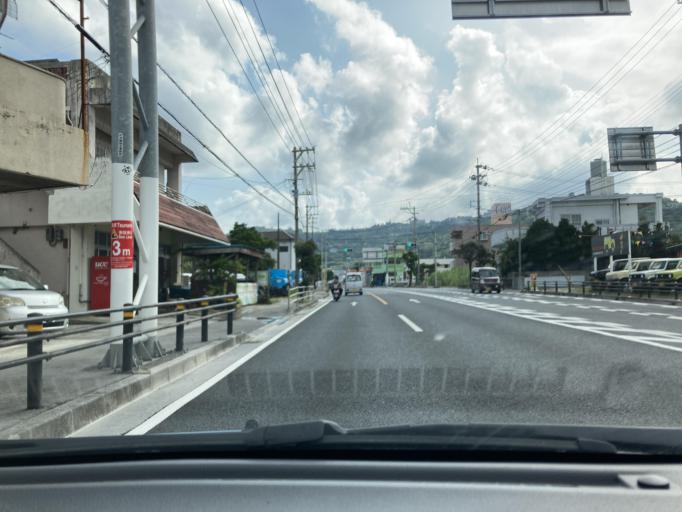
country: JP
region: Okinawa
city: Okinawa
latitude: 26.3014
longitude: 127.8092
